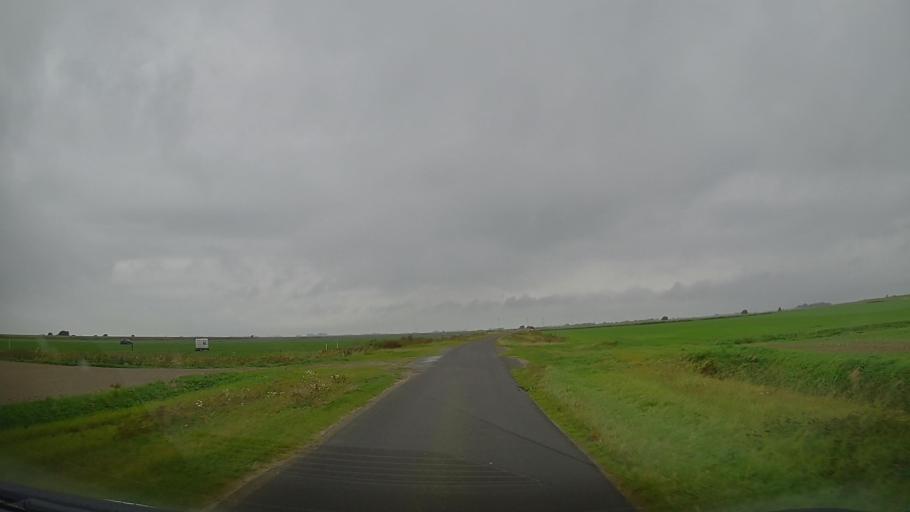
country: DE
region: Schleswig-Holstein
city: Friedrichsgabekoog
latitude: 54.1129
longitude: 8.9810
